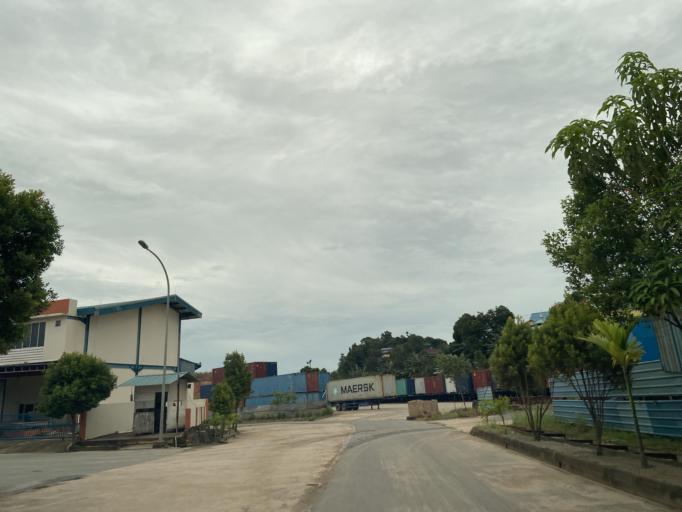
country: SG
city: Singapore
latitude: 1.1652
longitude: 104.0195
